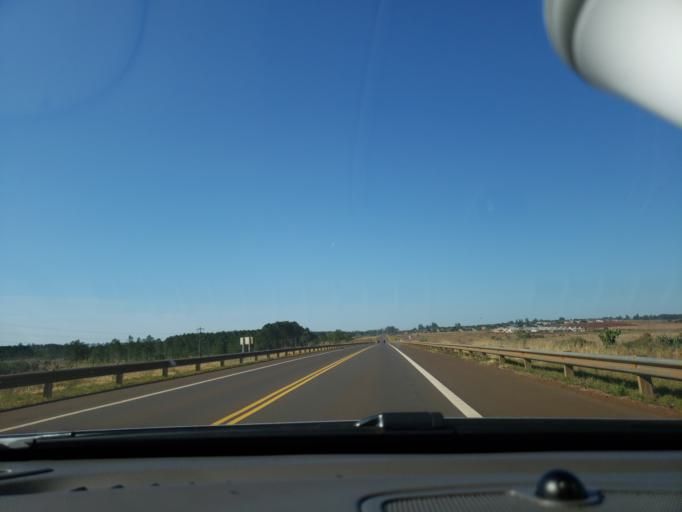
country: AR
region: Misiones
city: Garupa
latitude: -27.4644
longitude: -55.8939
